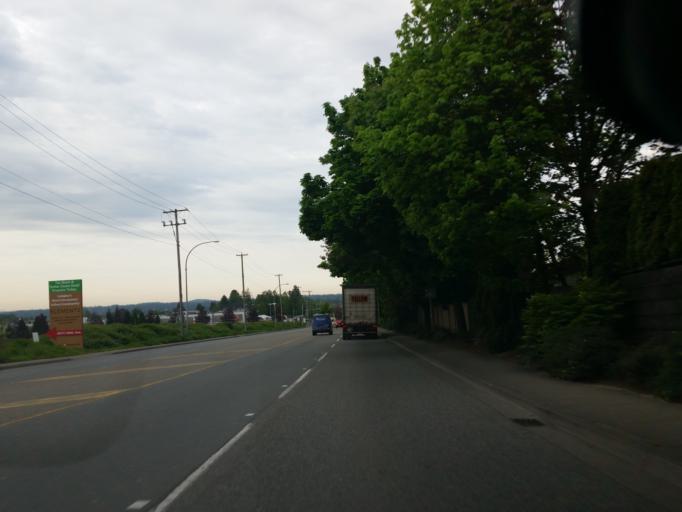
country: CA
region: British Columbia
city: Langley
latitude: 49.1258
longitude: -122.6687
